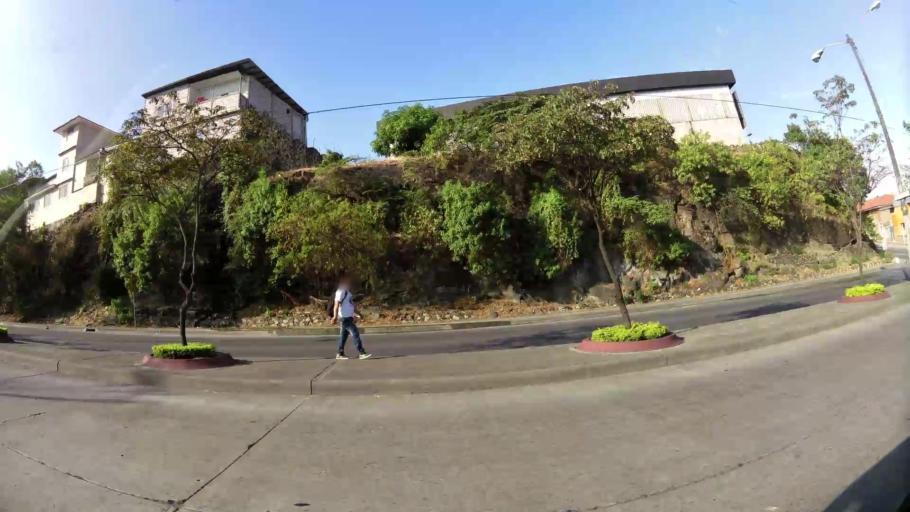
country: EC
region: Guayas
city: Guayaquil
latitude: -2.1601
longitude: -79.9121
